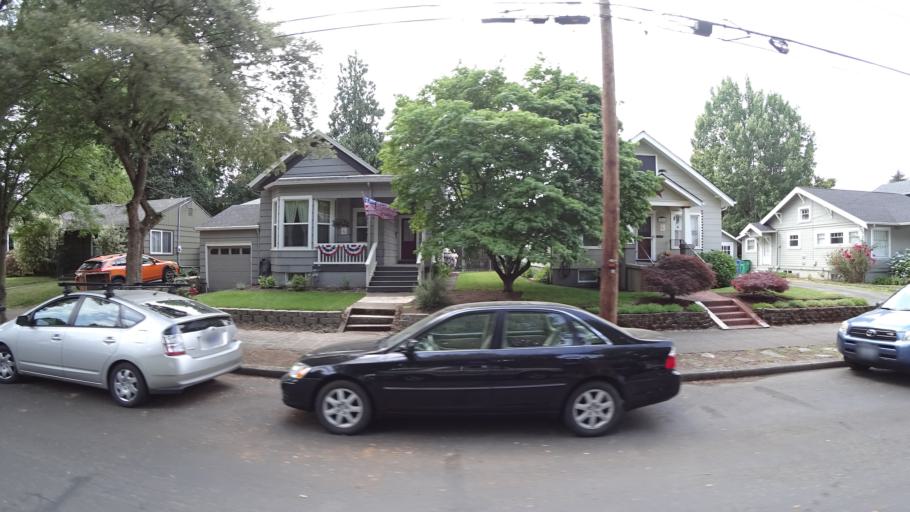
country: US
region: Oregon
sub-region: Multnomah County
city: Portland
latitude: 45.4946
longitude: -122.6514
